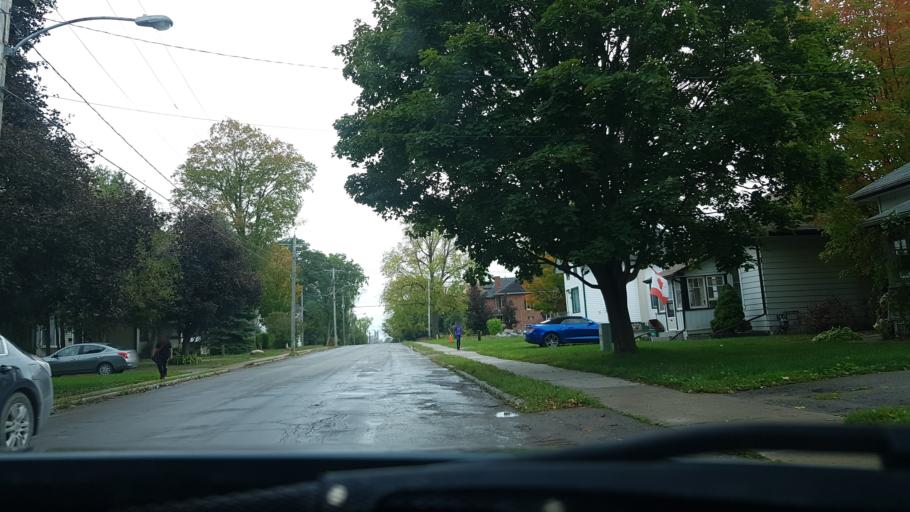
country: CA
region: Ontario
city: Omemee
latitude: 44.3642
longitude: -78.7413
